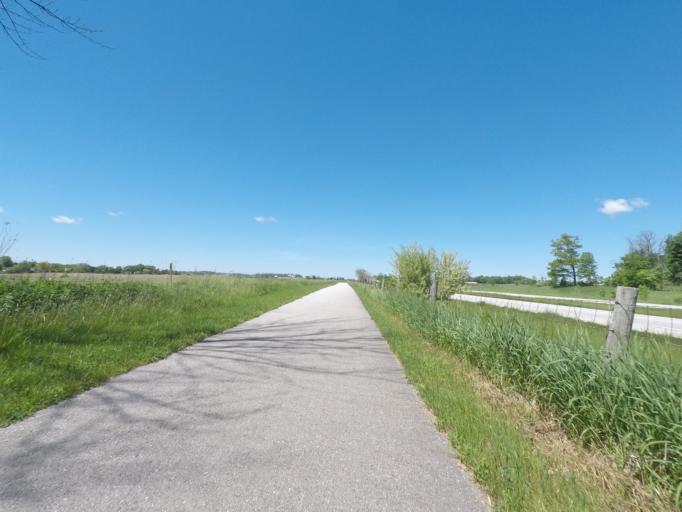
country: US
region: Wisconsin
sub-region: Sheboygan County
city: Sheboygan Falls
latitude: 43.7494
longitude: -87.8100
